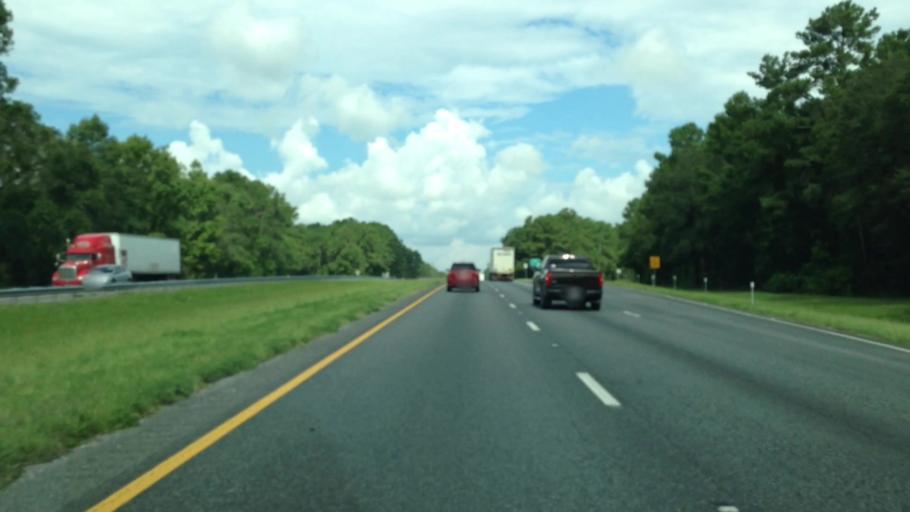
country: US
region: Florida
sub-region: Suwannee County
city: Wellborn
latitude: 30.2778
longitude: -82.8121
